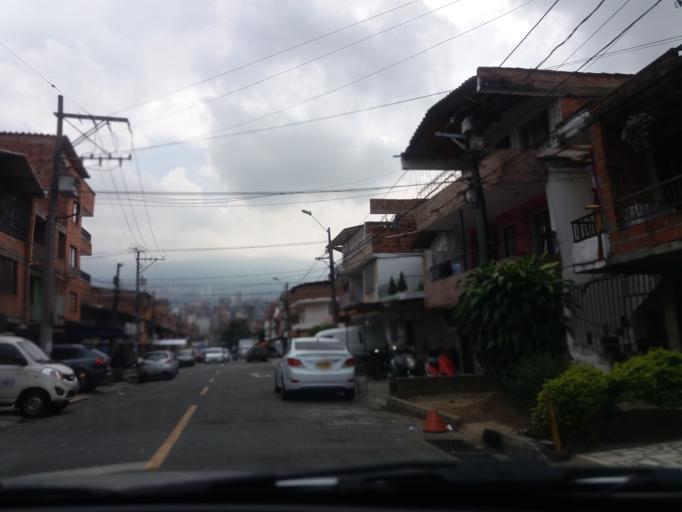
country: CO
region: Antioquia
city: Itagui
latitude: 6.2065
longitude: -75.5835
